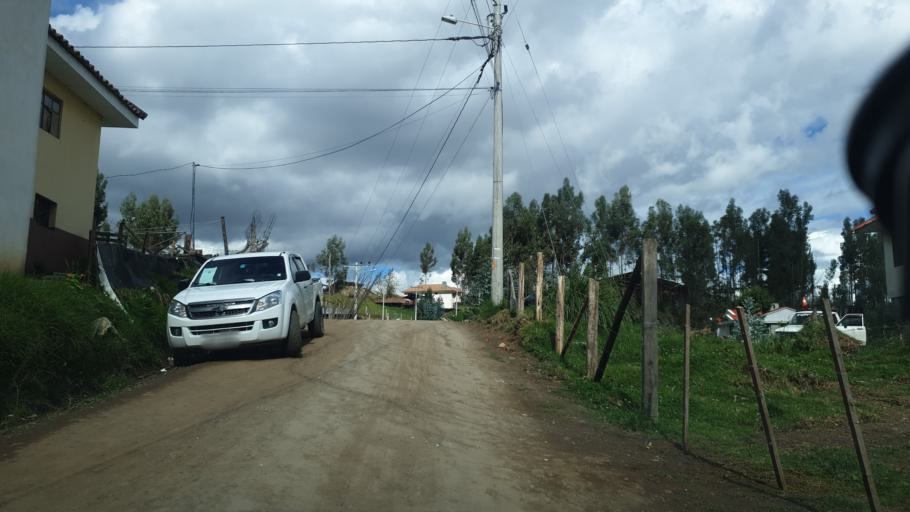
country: EC
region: Azuay
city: Cuenca
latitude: -2.8584
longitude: -79.0424
